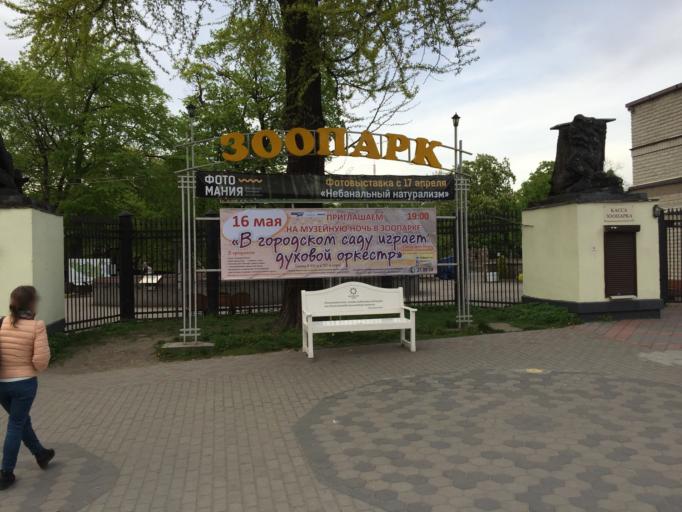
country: RU
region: Kaliningrad
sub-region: Gorod Kaliningrad
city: Kaliningrad
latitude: 54.7201
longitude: 20.4878
